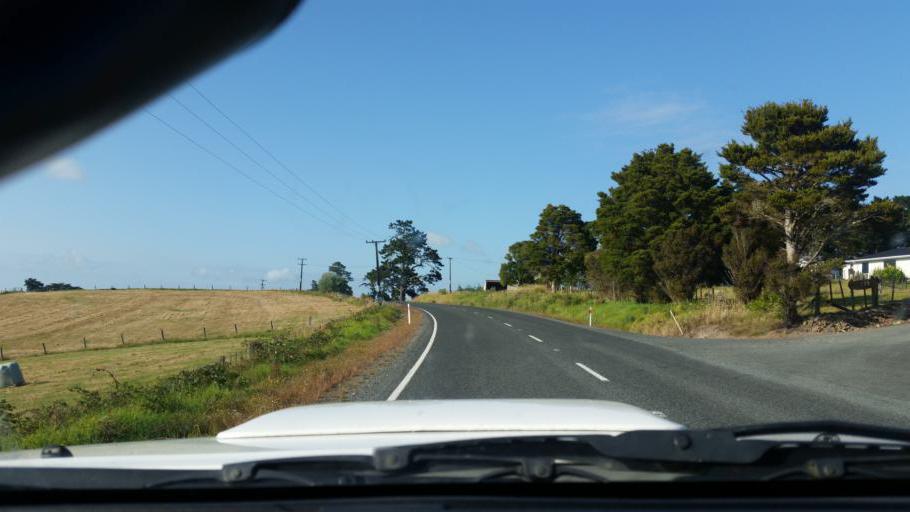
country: NZ
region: Northland
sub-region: Whangarei
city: Ruakaka
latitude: -36.1256
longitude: 174.2313
